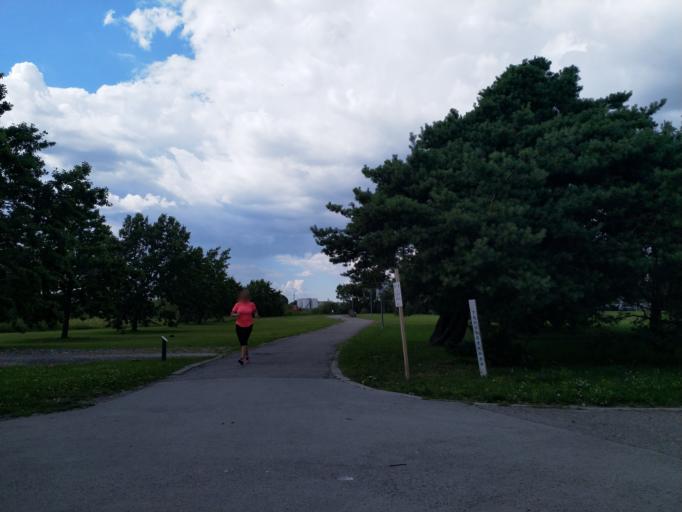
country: EE
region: Paernumaa
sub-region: Paernu linn
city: Parnu
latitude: 58.3820
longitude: 24.4849
